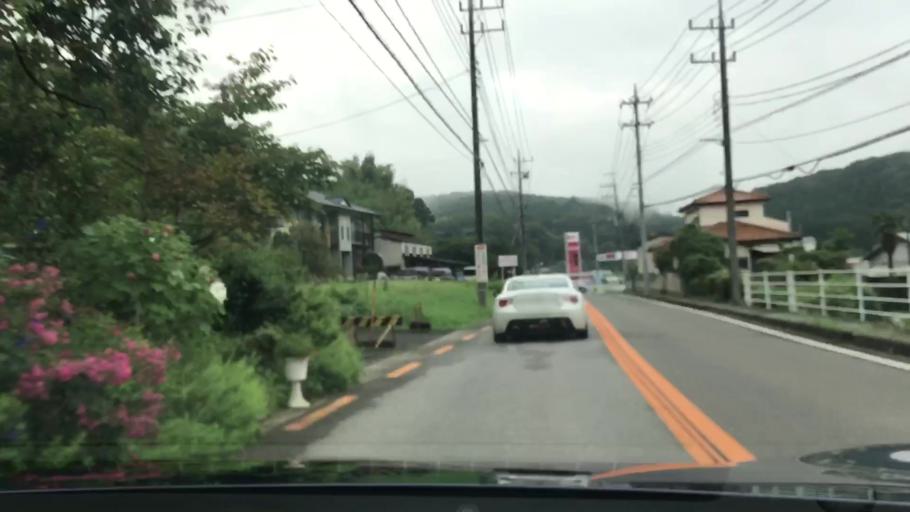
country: JP
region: Tochigi
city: Motegi
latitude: 36.5336
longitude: 140.1987
